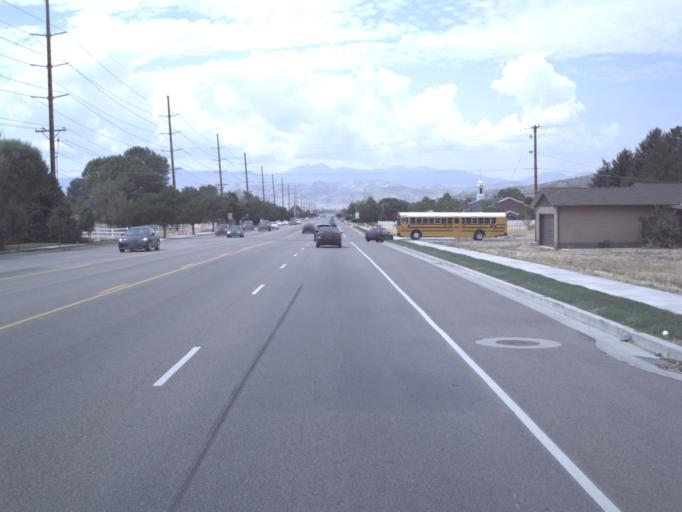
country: US
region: Utah
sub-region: Utah County
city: Alpine
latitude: 40.4320
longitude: -111.7946
